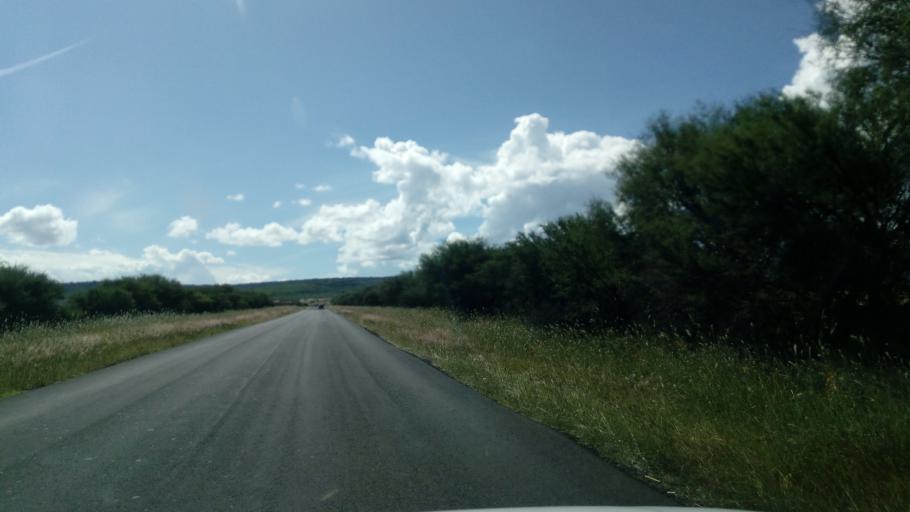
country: MX
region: Durango
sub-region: Durango
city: Jose Refugio Salcido
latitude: 23.8573
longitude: -104.4742
